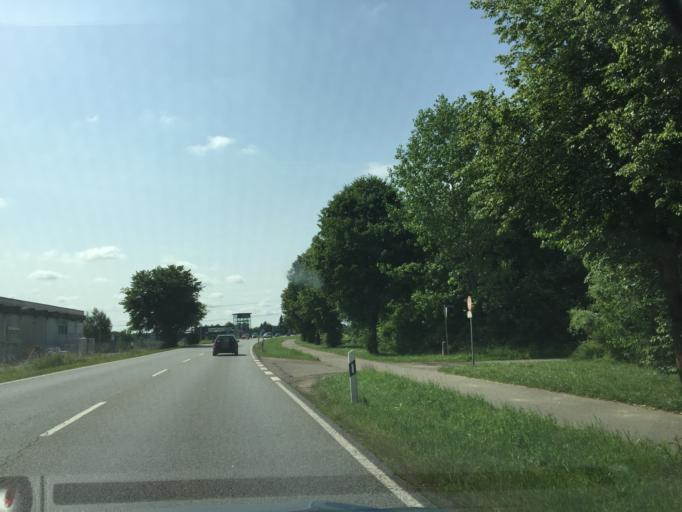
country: DE
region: Bavaria
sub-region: Swabia
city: Senden
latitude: 48.3175
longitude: 10.0524
